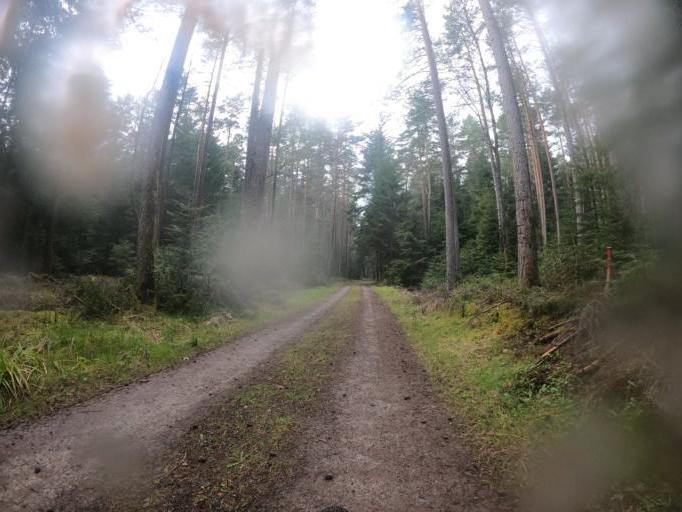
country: DE
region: Baden-Wuerttemberg
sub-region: Karlsruhe Region
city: Oberreichenbach
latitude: 48.7027
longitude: 8.6306
